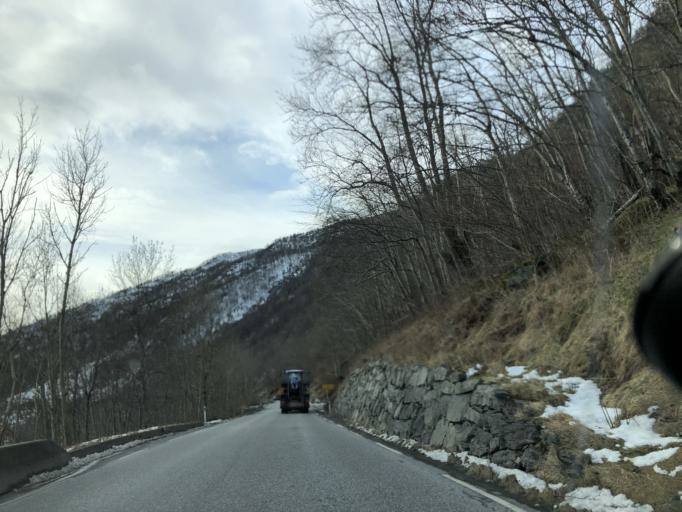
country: NO
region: Hordaland
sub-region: Etne
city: Etne
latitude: 59.7070
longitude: 6.0492
